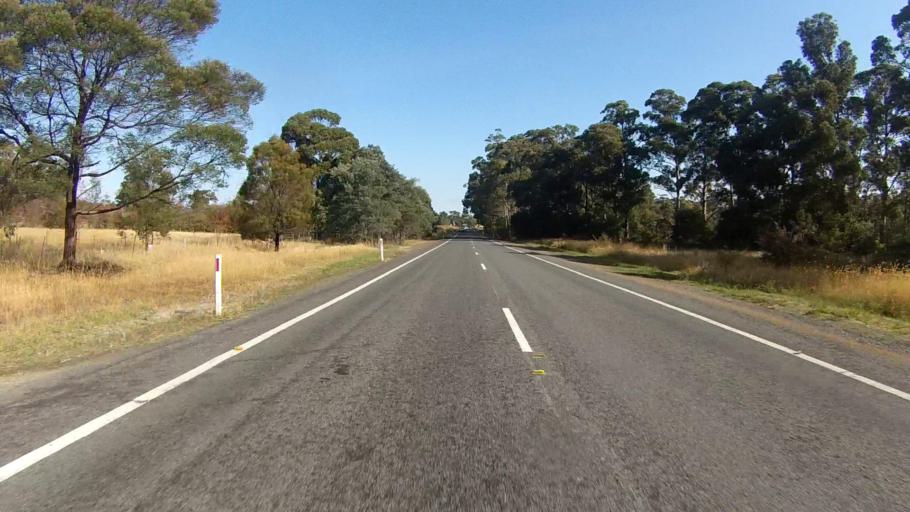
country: AU
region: Tasmania
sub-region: Sorell
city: Sorell
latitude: -42.6952
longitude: 147.5262
